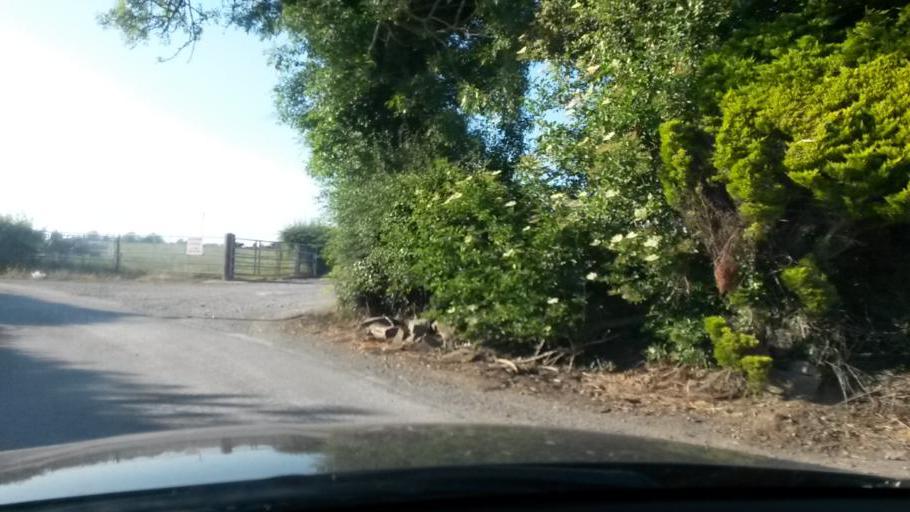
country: IE
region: Leinster
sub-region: Fingal County
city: Swords
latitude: 53.5031
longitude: -6.2909
